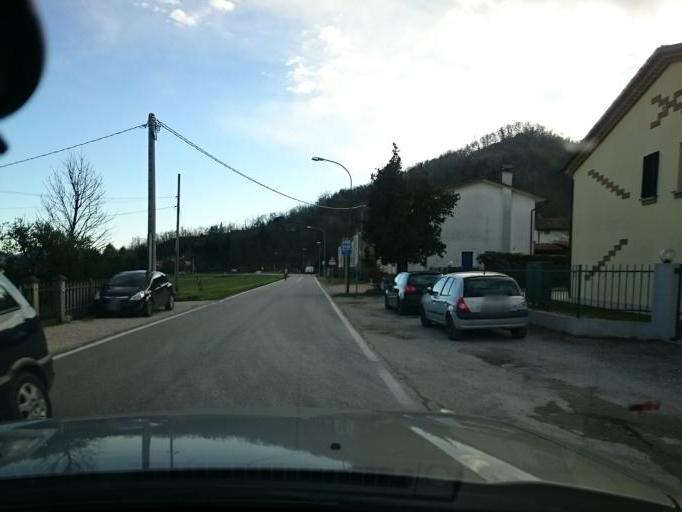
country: IT
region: Veneto
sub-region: Provincia di Padova
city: Torreglia
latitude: 45.3514
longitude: 11.7358
